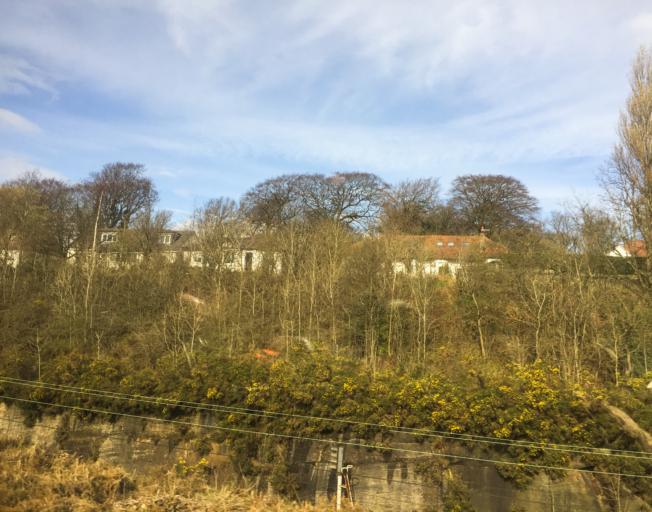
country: GB
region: Scotland
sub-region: East Dunbartonshire
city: Bearsden
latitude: 55.8993
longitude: -4.3239
